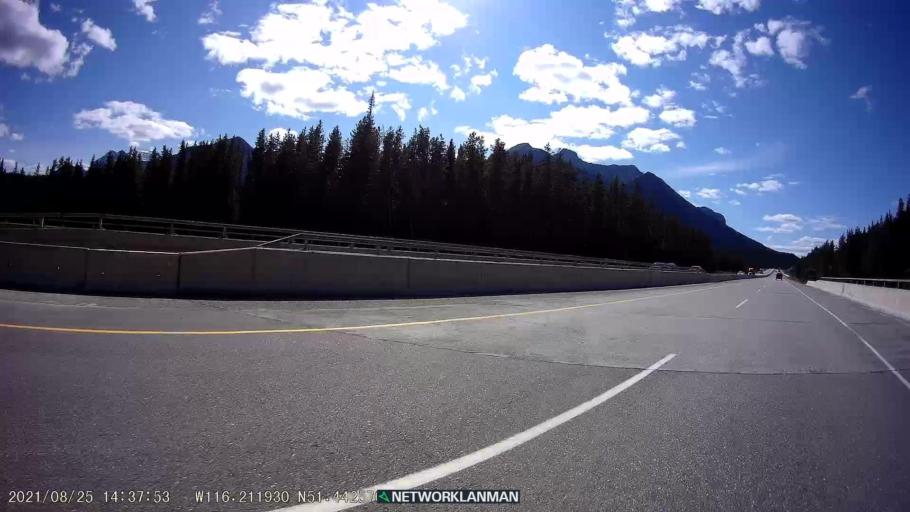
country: CA
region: Alberta
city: Lake Louise
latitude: 51.4422
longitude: -116.2127
